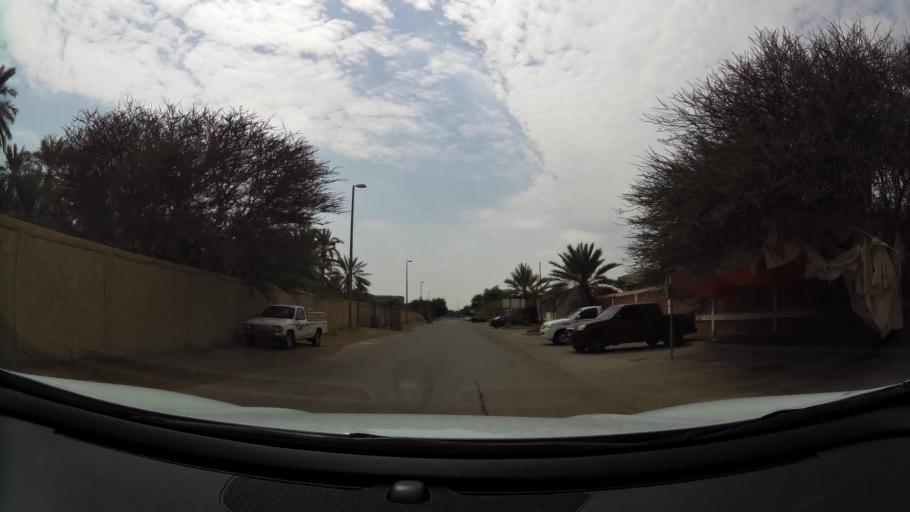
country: OM
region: Al Buraimi
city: Al Buraymi
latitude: 24.2167
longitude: 55.7962
